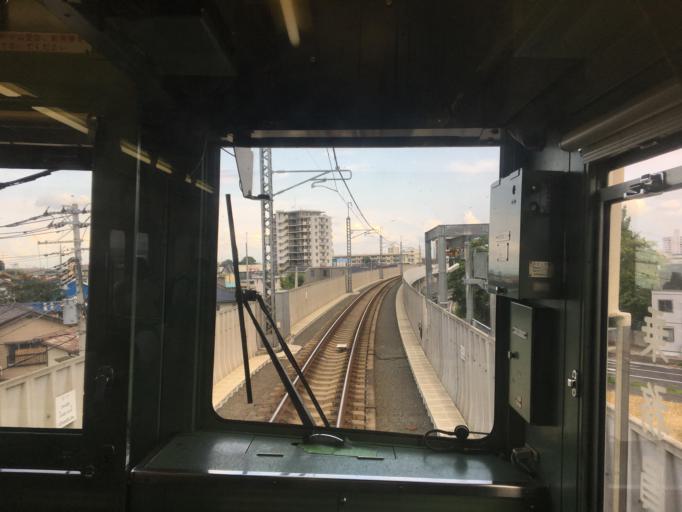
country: JP
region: Gunma
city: Isesaki
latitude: 36.3253
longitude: 139.1987
